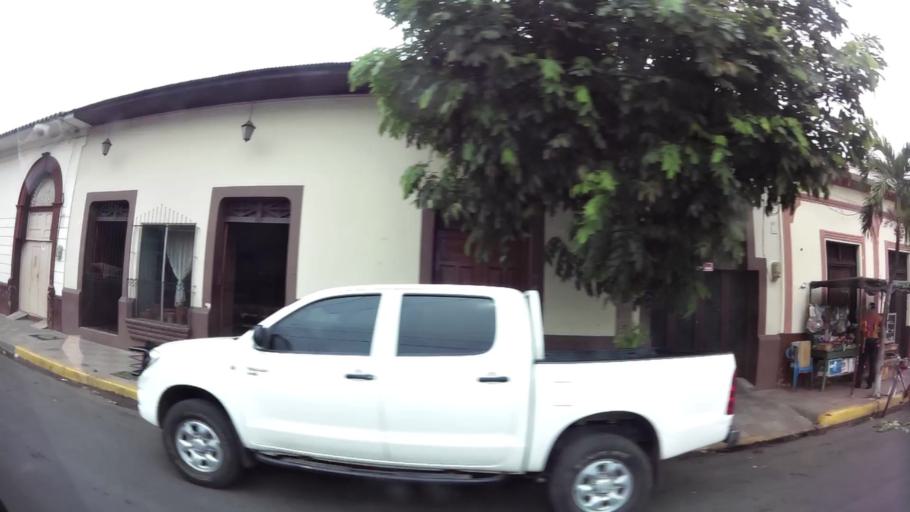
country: NI
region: Leon
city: Leon
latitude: 12.4393
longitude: -86.8759
